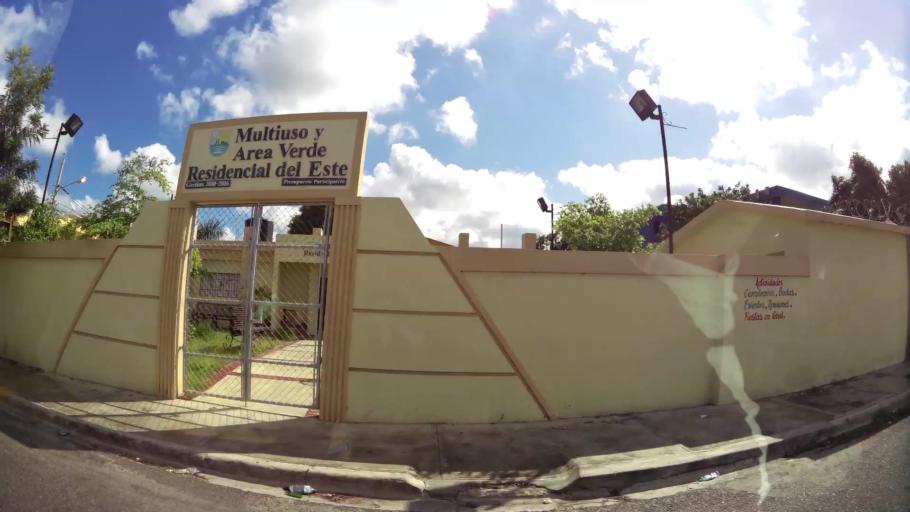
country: DO
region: Santo Domingo
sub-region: Santo Domingo
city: Santo Domingo Este
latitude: 18.5075
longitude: -69.8499
